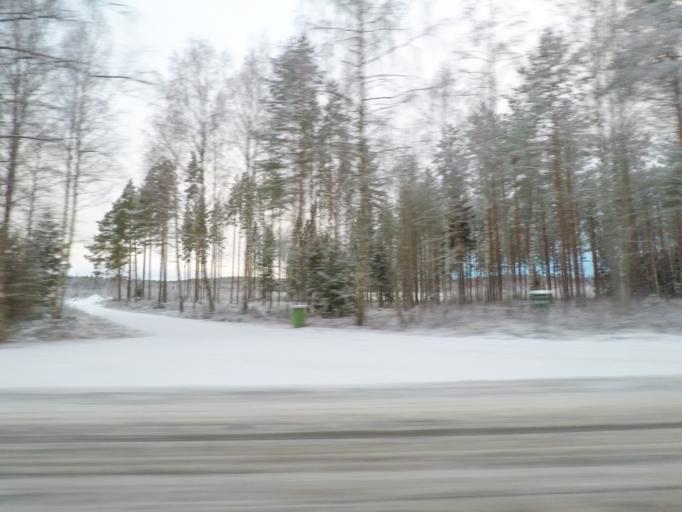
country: FI
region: Uusimaa
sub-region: Helsinki
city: Sammatti
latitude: 60.2856
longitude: 23.8028
